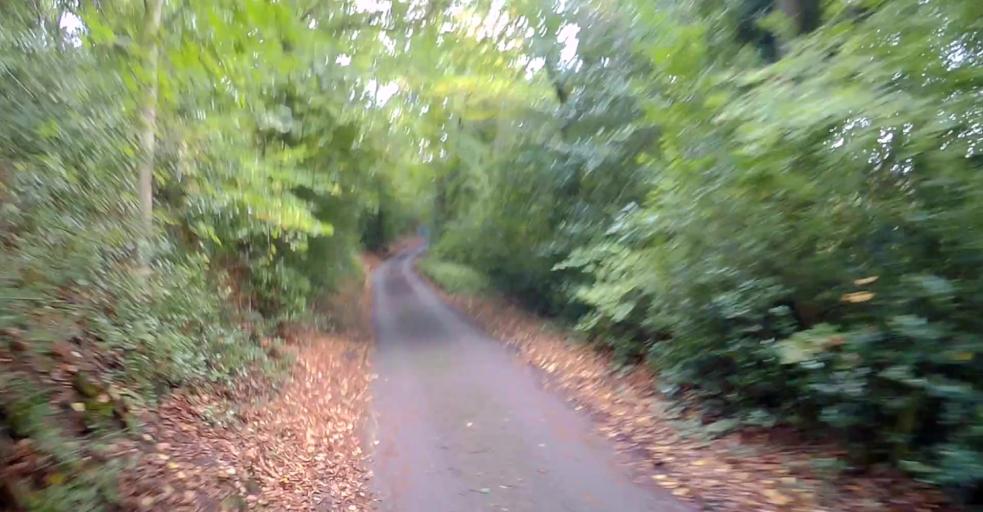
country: GB
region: England
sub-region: Surrey
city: Elstead
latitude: 51.1864
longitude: -0.7374
